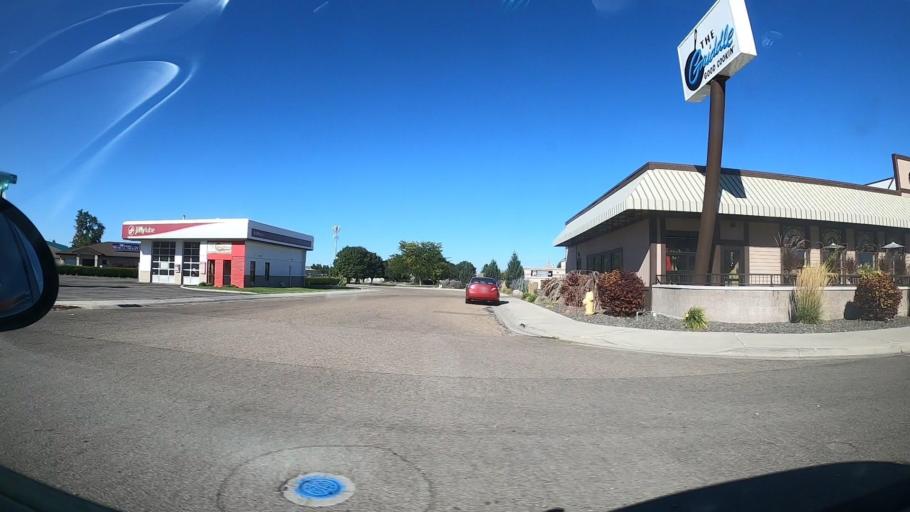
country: US
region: Idaho
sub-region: Canyon County
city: Nampa
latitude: 43.5986
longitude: -116.5930
